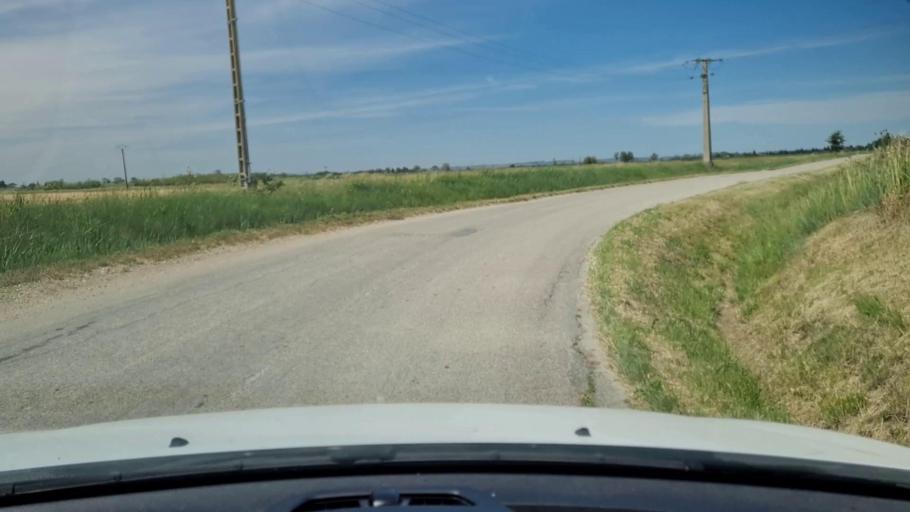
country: FR
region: Languedoc-Roussillon
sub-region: Departement du Gard
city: Saint-Gilles
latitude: 43.6105
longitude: 4.4262
